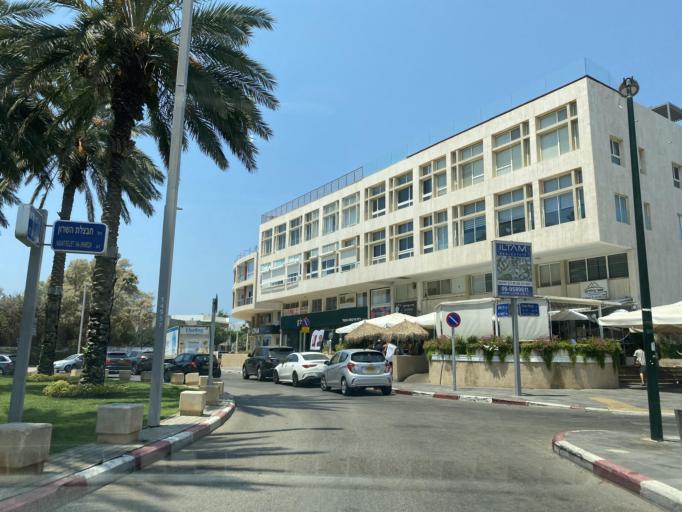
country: IL
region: Tel Aviv
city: Herzliya Pituah
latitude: 32.1796
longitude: 34.8050
